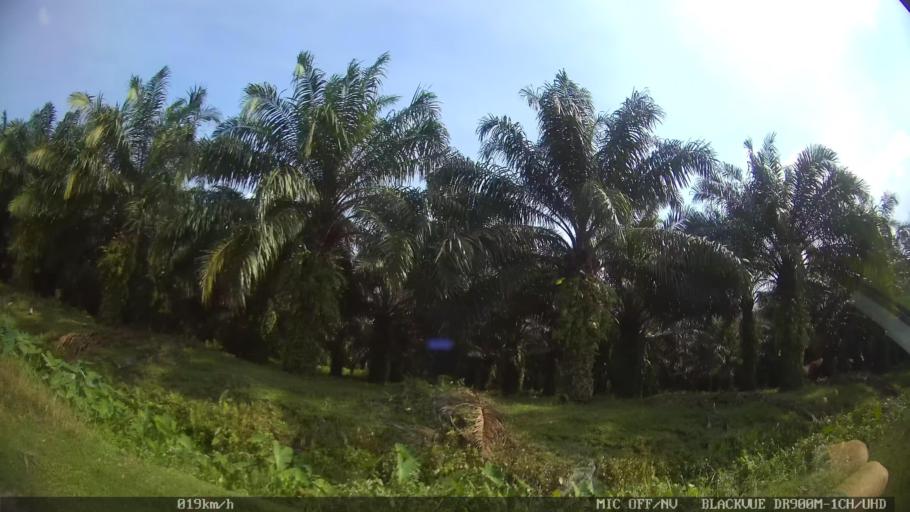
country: ID
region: North Sumatra
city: Binjai
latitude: 3.6426
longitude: 98.5264
